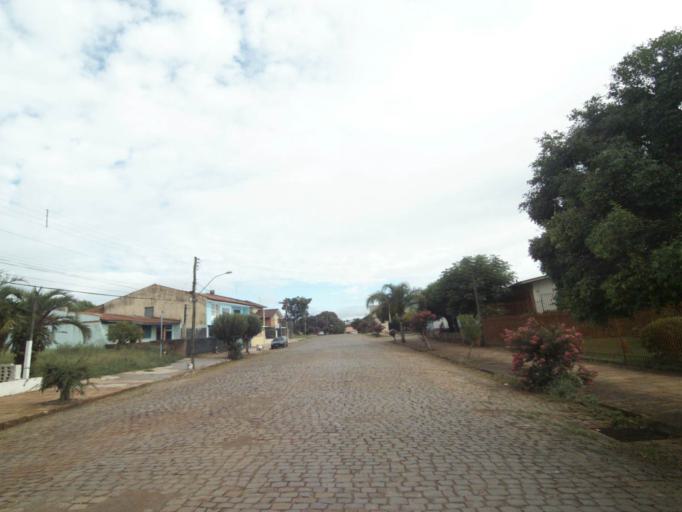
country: BR
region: Rio Grande do Sul
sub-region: Lagoa Vermelha
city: Lagoa Vermelha
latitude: -28.2105
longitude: -51.5167
